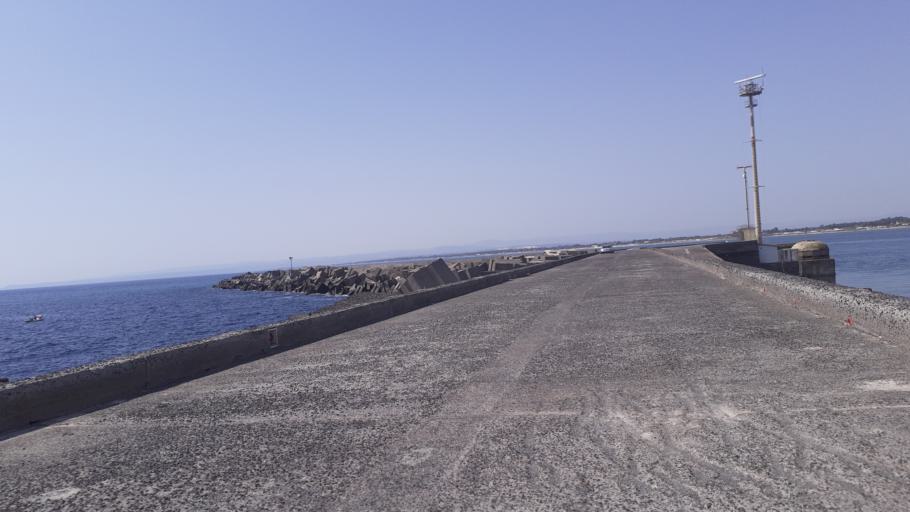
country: IT
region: Sicily
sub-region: Catania
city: Catania
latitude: 37.4880
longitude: 15.1000
